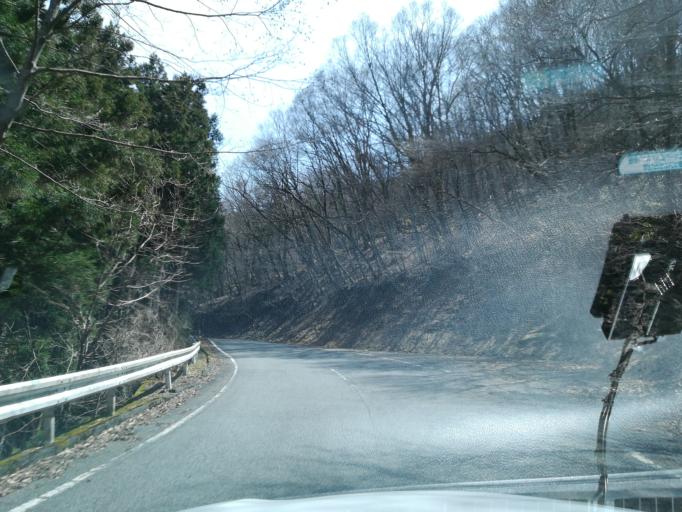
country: JP
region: Tokushima
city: Wakimachi
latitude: 33.8835
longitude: 134.0512
